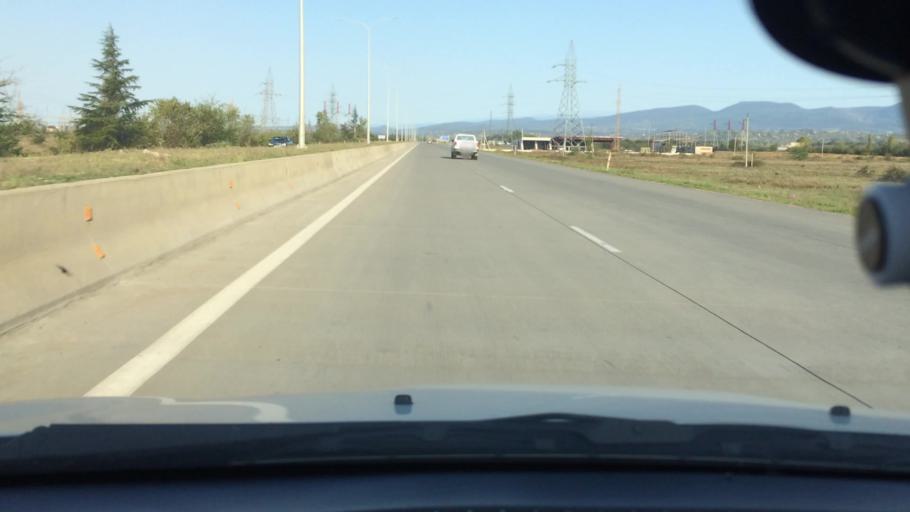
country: GE
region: Imereti
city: Zestap'oni
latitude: 42.1439
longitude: 42.9691
